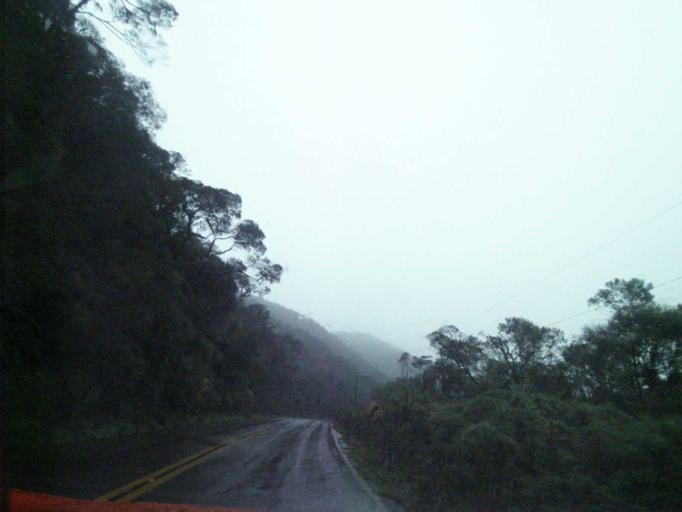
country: BR
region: Santa Catarina
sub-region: Anitapolis
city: Anitapolis
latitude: -27.7530
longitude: -49.0354
